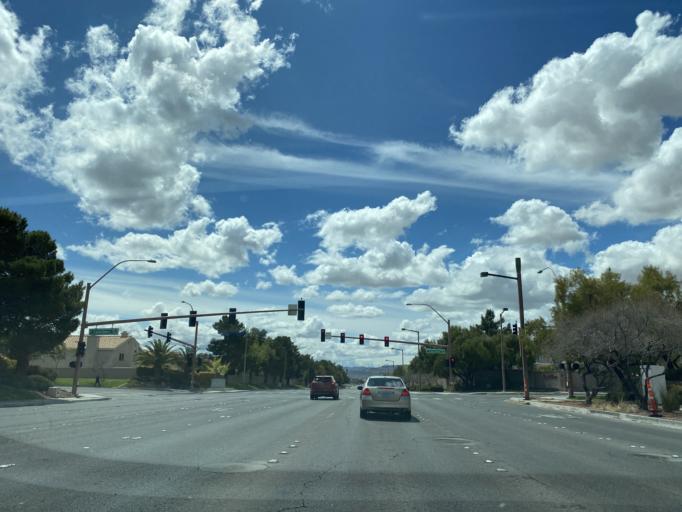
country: US
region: Nevada
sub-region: Clark County
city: Summerlin South
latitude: 36.1377
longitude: -115.3154
